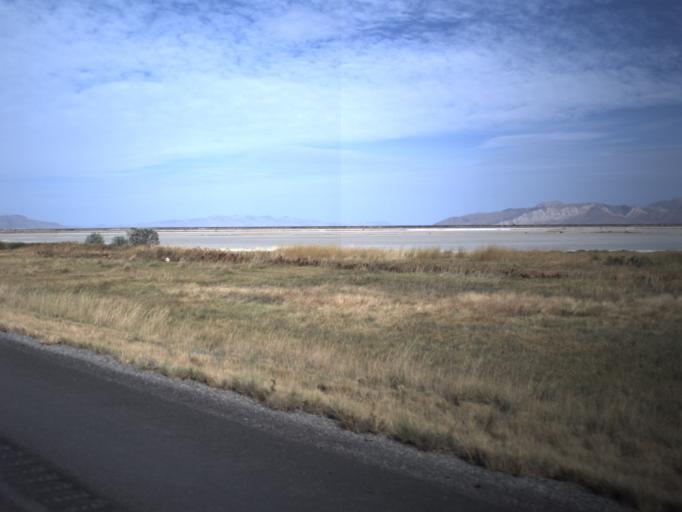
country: US
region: Utah
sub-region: Tooele County
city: Stansbury park
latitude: 40.6626
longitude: -112.3408
